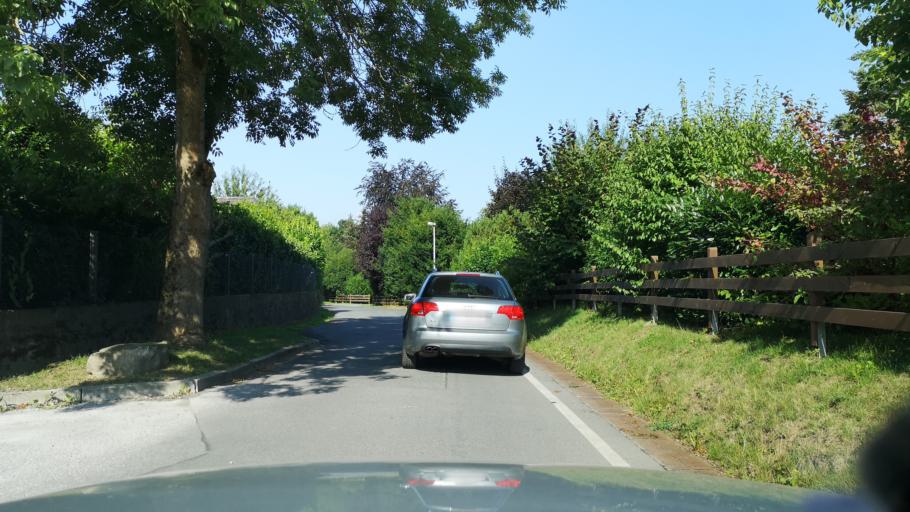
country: DE
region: North Rhine-Westphalia
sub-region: Regierungsbezirk Arnsberg
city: Menden
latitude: 51.4609
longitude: 7.7932
